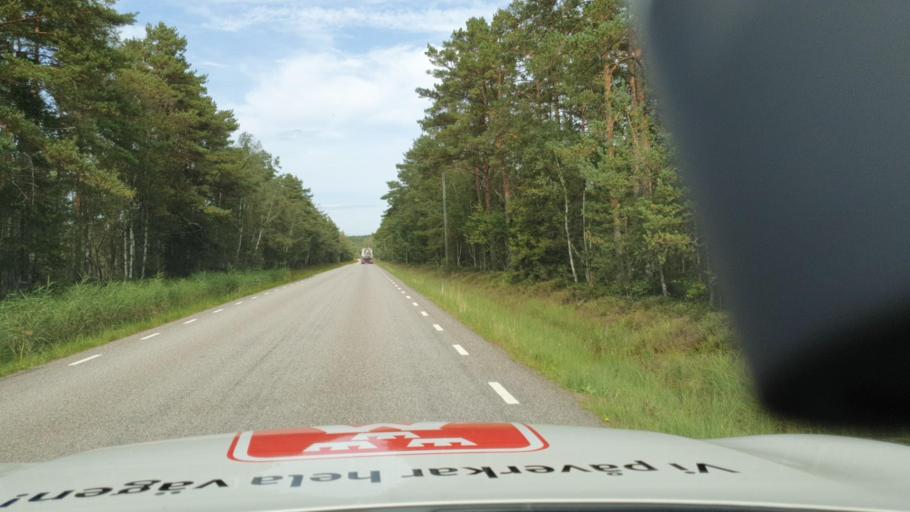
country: SE
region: Vaestra Goetaland
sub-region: Marks Kommun
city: Kinna
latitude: 57.4077
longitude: 12.6775
